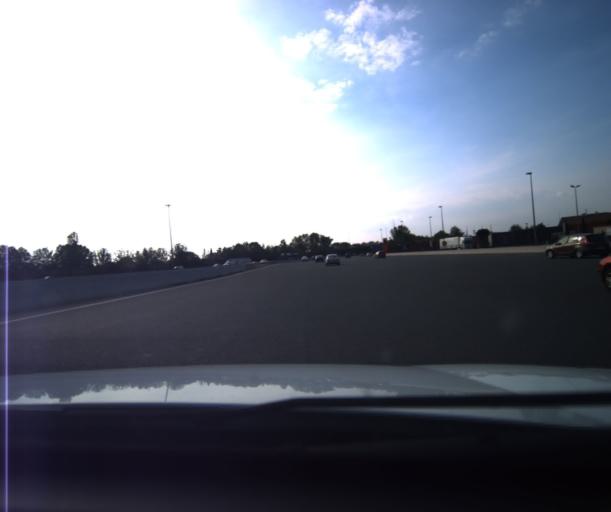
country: FR
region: Midi-Pyrenees
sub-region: Departement de la Haute-Garonne
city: Aucamville
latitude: 43.6589
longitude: 1.4271
